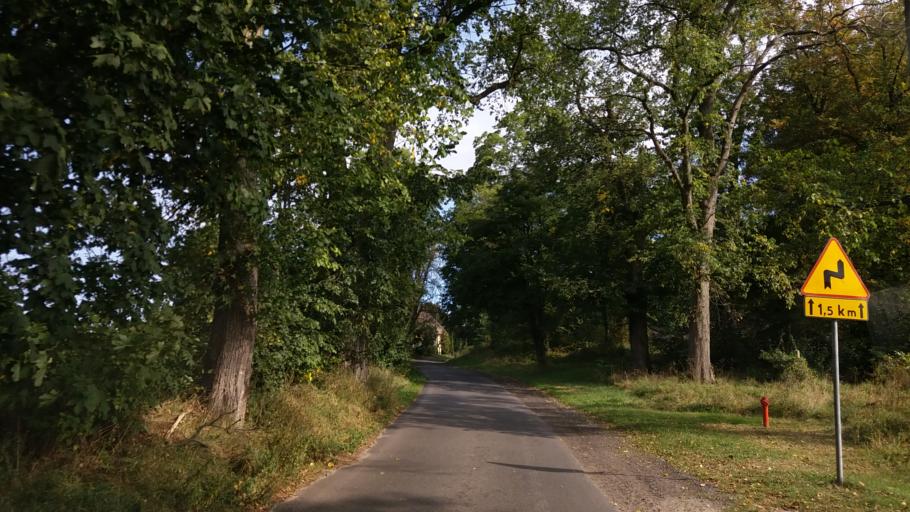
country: PL
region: West Pomeranian Voivodeship
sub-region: Powiat stargardzki
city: Suchan
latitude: 53.2316
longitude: 15.3480
